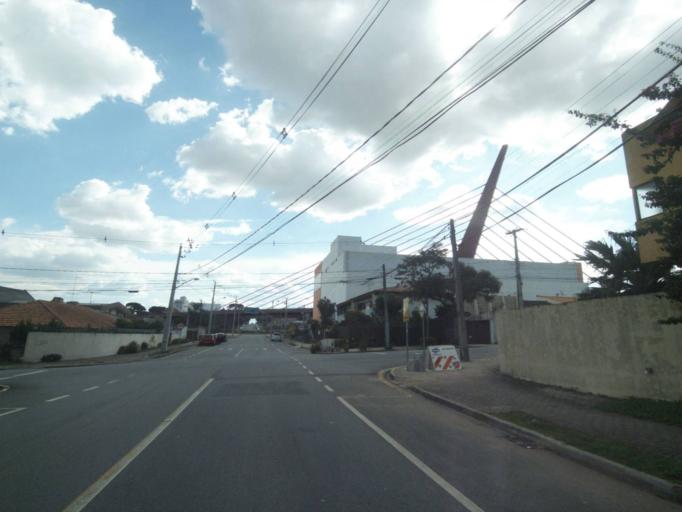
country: BR
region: Parana
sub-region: Pinhais
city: Pinhais
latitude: -25.4644
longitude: -49.2331
